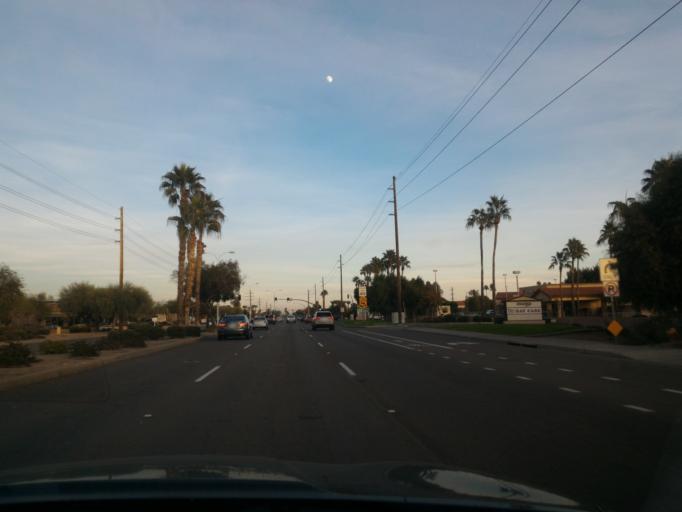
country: US
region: Arizona
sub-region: Maricopa County
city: Guadalupe
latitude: 33.3053
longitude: -111.9496
